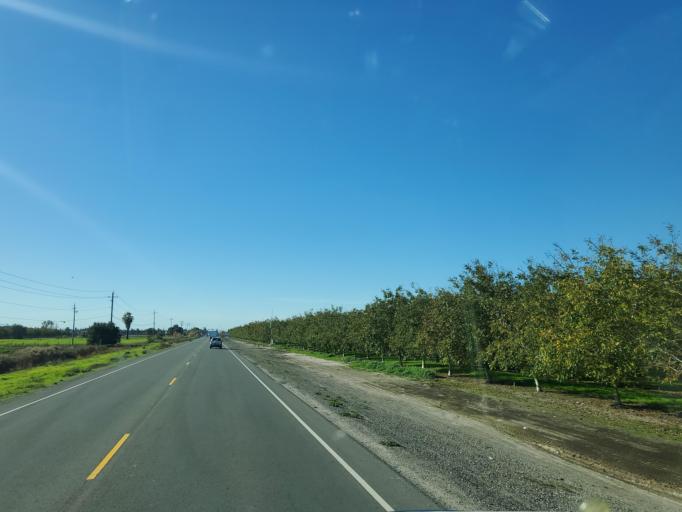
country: US
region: California
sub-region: San Joaquin County
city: Lincoln Village
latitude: 38.0576
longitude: -121.3041
